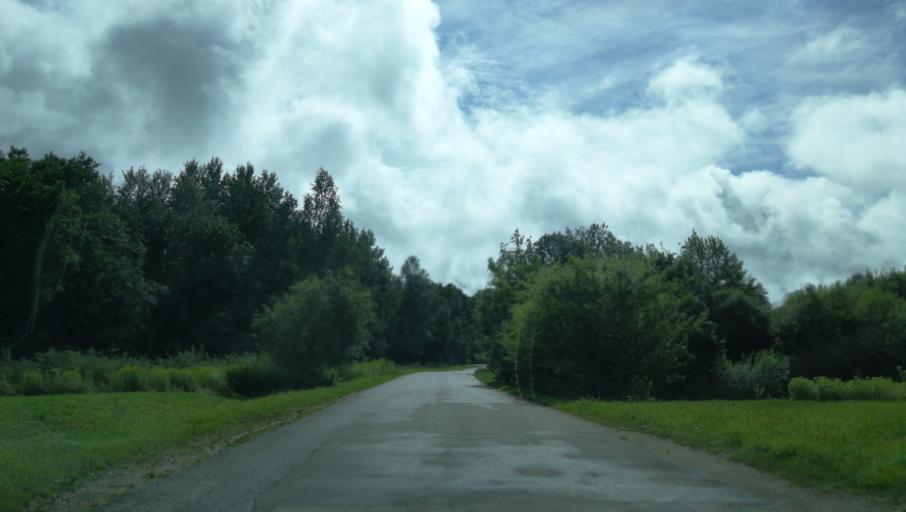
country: LV
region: Cesu Rajons
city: Cesis
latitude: 57.2978
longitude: 25.2613
